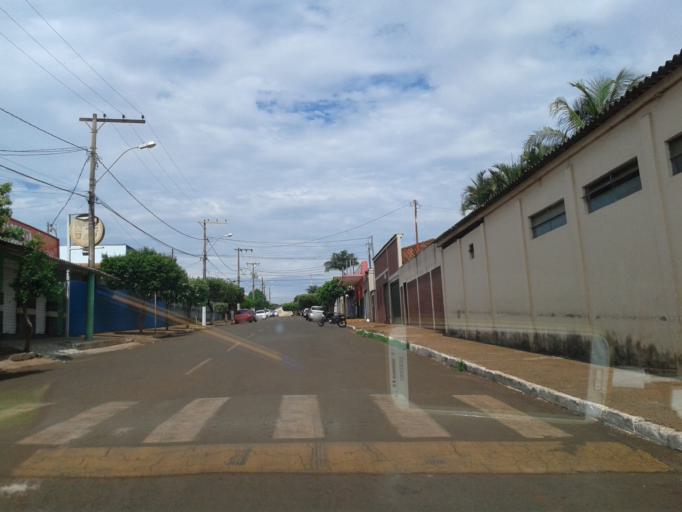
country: BR
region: Goias
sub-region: Itumbiara
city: Itumbiara
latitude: -18.4370
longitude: -49.1852
